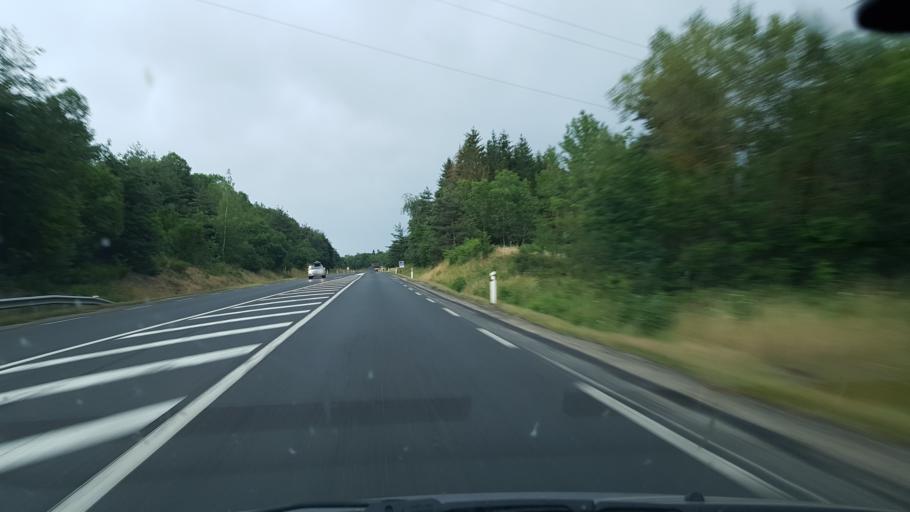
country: FR
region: Auvergne
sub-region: Departement de la Haute-Loire
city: Allegre
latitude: 45.1376
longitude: 3.6112
